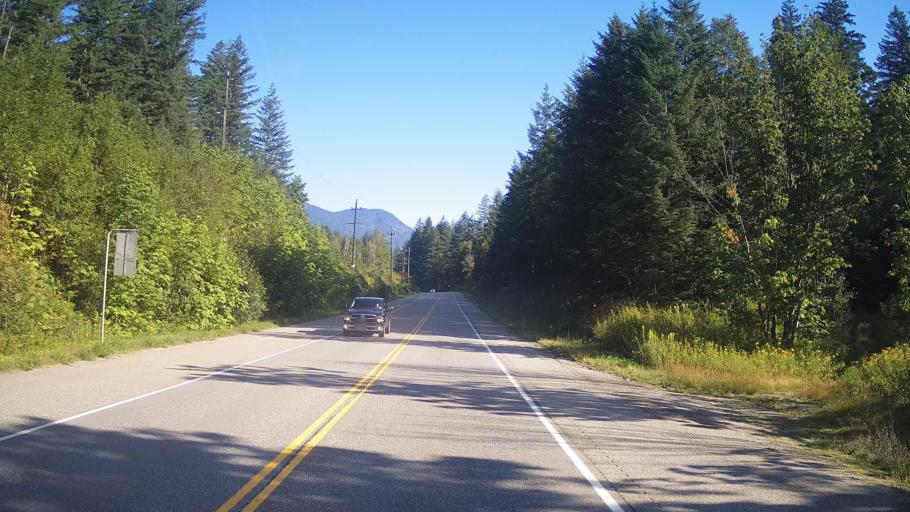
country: CA
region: British Columbia
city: Hope
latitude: 49.5101
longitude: -121.4176
